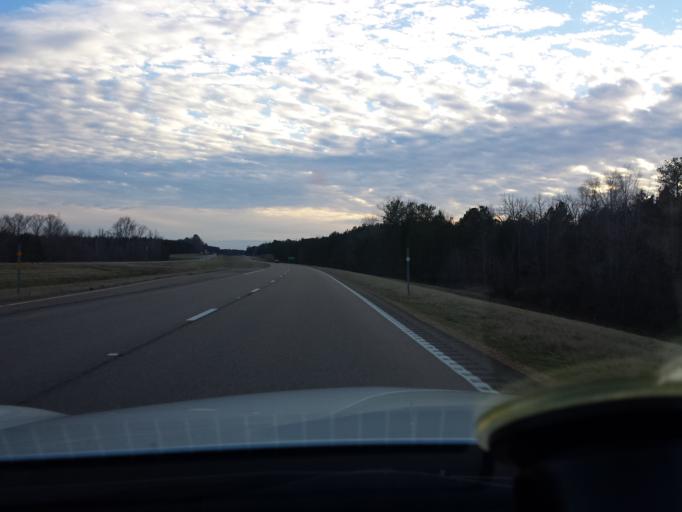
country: US
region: Mississippi
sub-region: Oktibbeha County
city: Starkville
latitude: 33.3817
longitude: -88.8703
